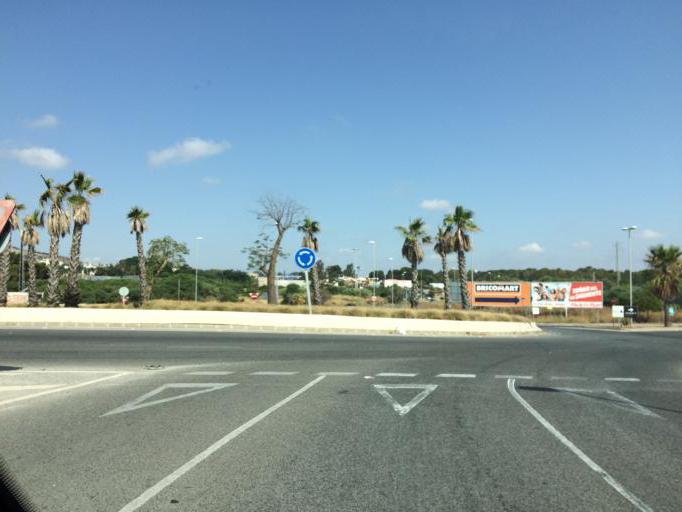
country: ES
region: Andalusia
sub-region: Provincia de Malaga
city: Torremolinos
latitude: 36.6550
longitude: -4.4819
